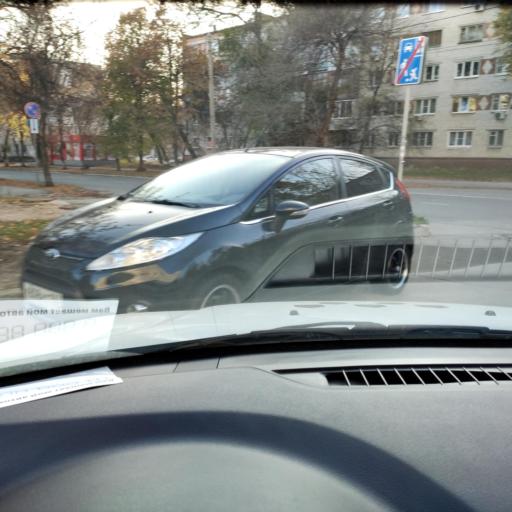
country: RU
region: Samara
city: Tol'yatti
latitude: 53.5043
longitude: 49.4085
